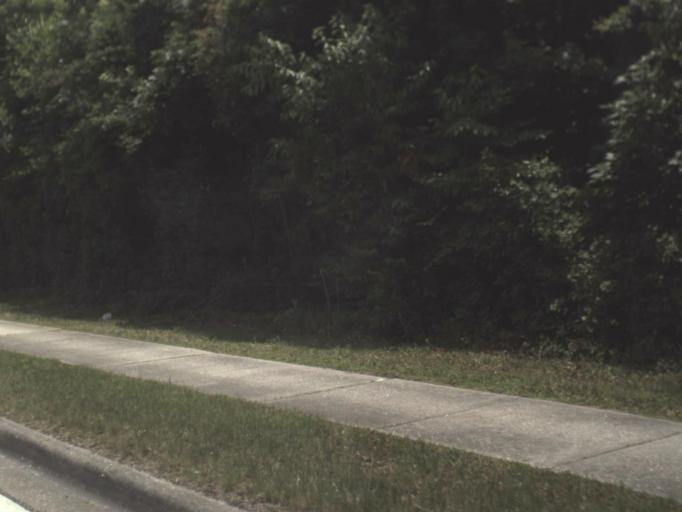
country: US
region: Florida
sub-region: Nassau County
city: Fernandina Beach
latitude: 30.6323
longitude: -81.4651
